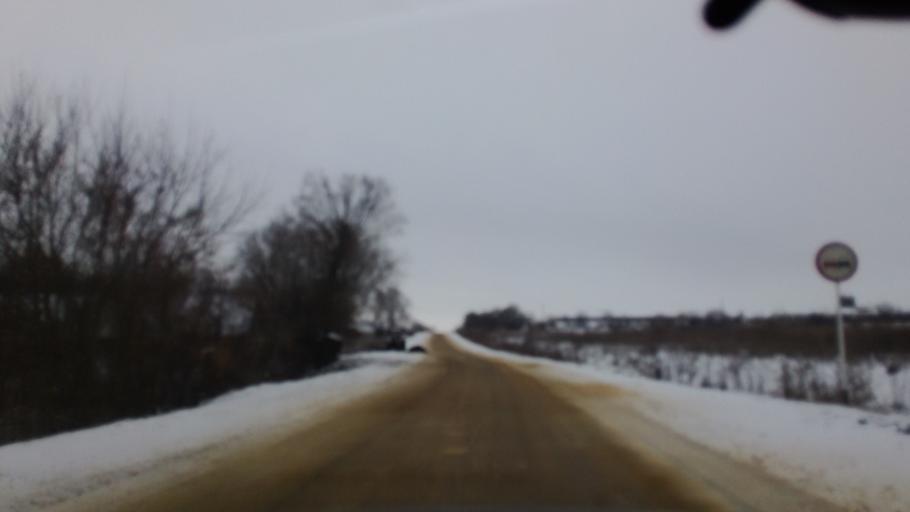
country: RU
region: Tula
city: Bogoroditsk
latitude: 53.7576
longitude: 37.9888
